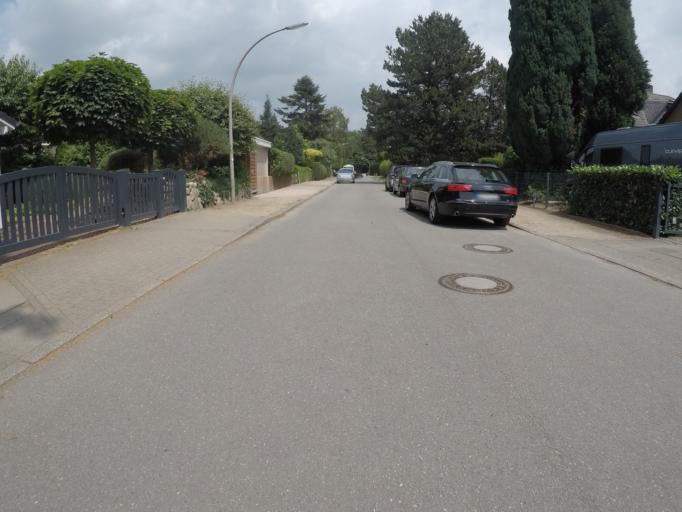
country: DE
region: Schleswig-Holstein
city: Bonningstedt
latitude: 53.6372
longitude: 9.9395
